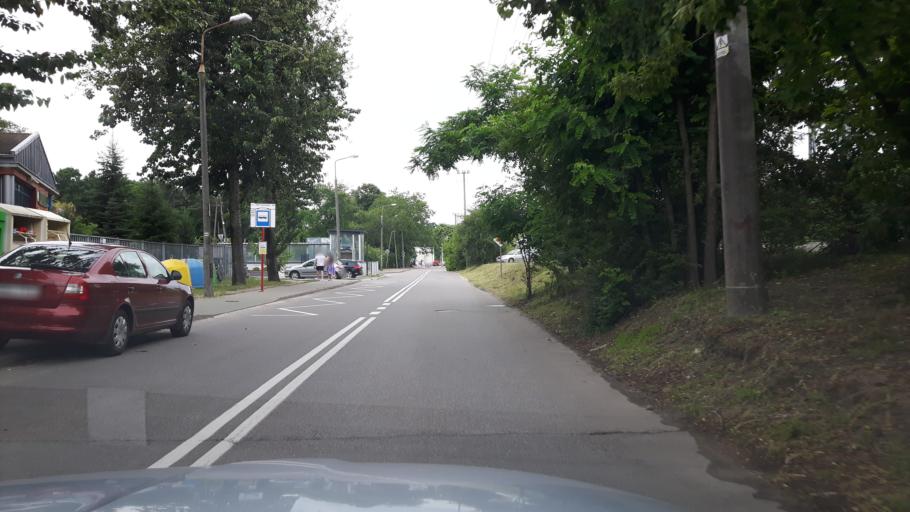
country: PL
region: Masovian Voivodeship
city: Zielonka
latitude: 52.3109
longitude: 21.1566
